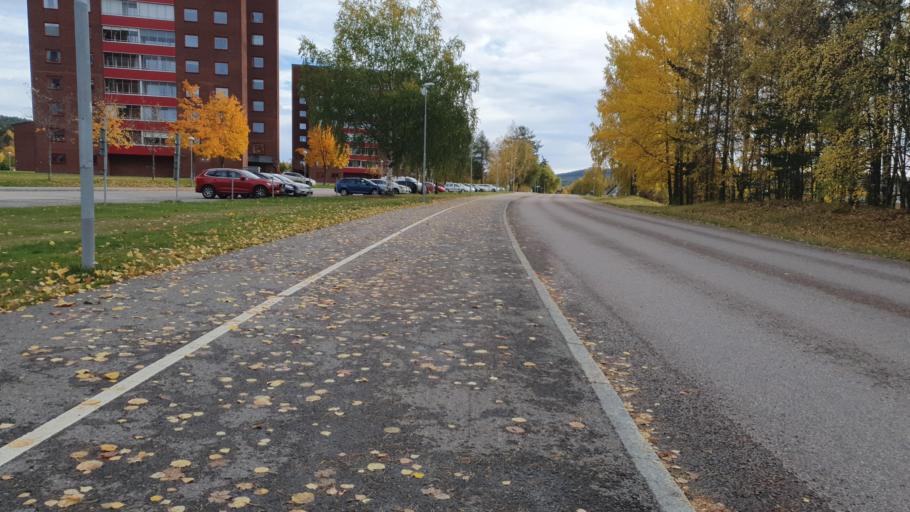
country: SE
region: Vaesternorrland
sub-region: Sundsvalls Kommun
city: Sundsvall
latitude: 62.4040
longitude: 17.2501
